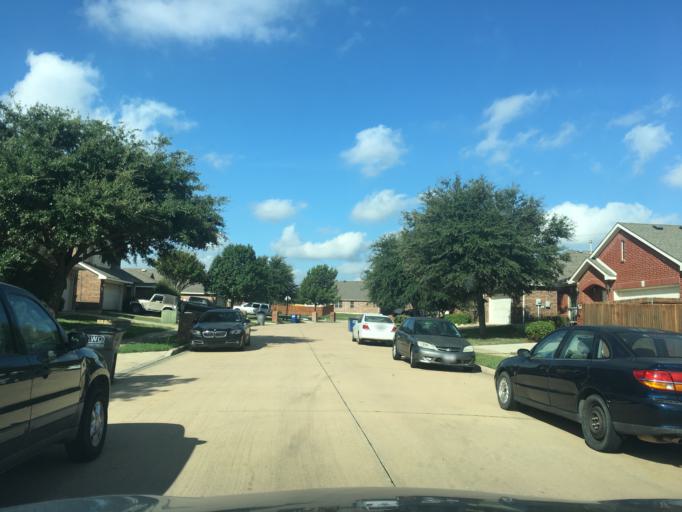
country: US
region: Texas
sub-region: Dallas County
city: Sachse
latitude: 32.9656
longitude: -96.5751
